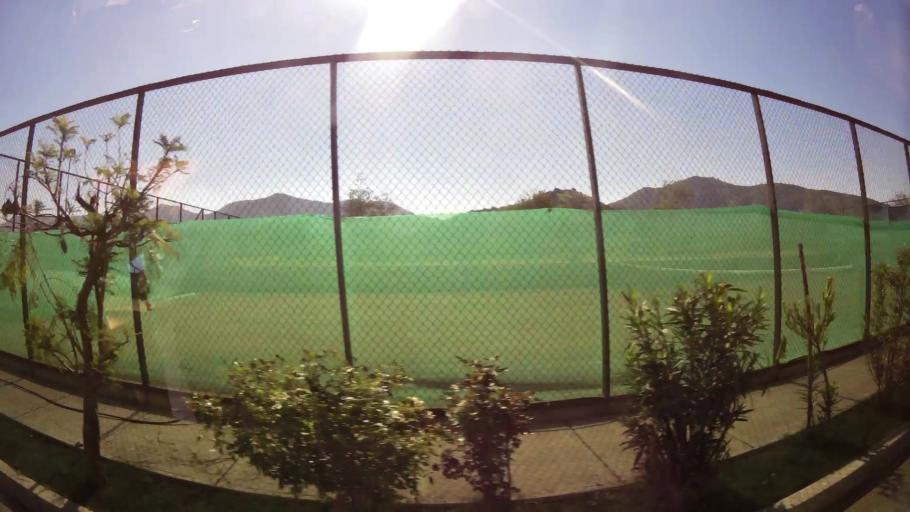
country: CL
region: Santiago Metropolitan
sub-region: Provincia de Talagante
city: Penaflor
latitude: -33.6044
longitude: -70.9064
